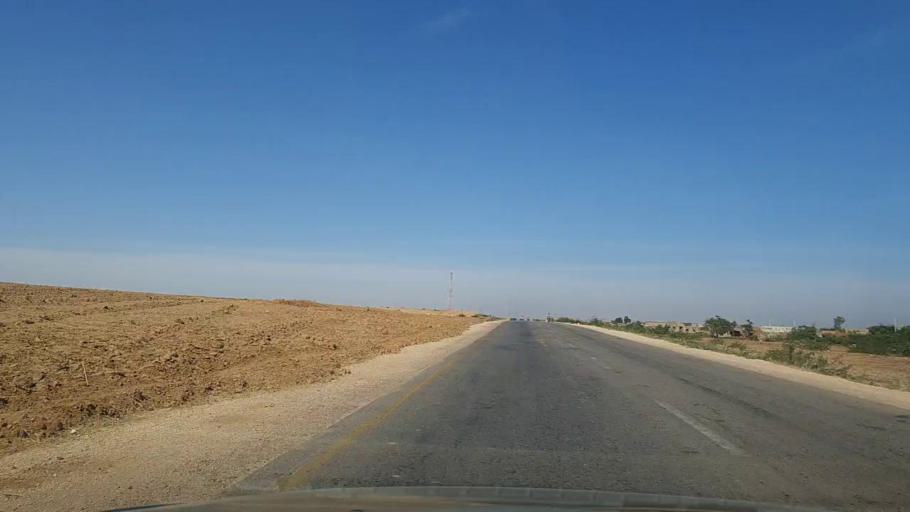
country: PK
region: Sindh
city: Kotri
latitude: 25.1934
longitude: 68.2385
